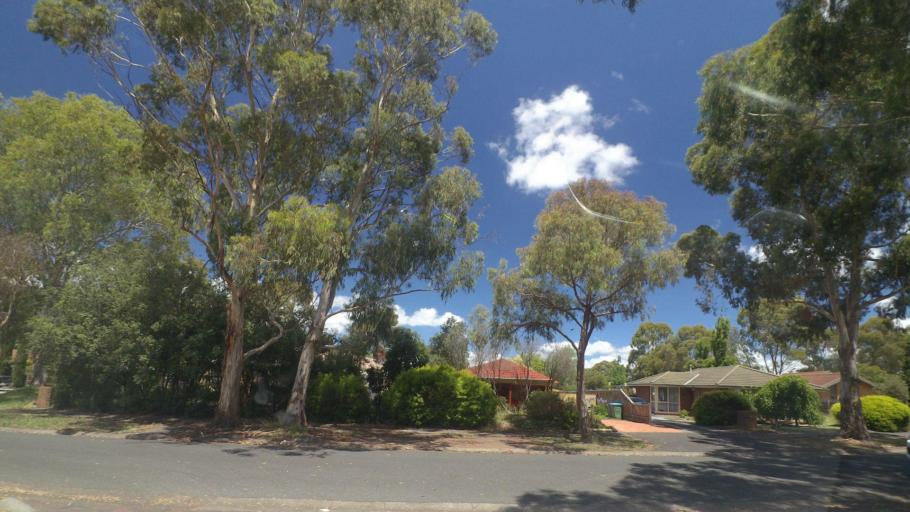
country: AU
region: Victoria
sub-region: Maroondah
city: Croydon South
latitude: -37.8192
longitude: 145.2815
